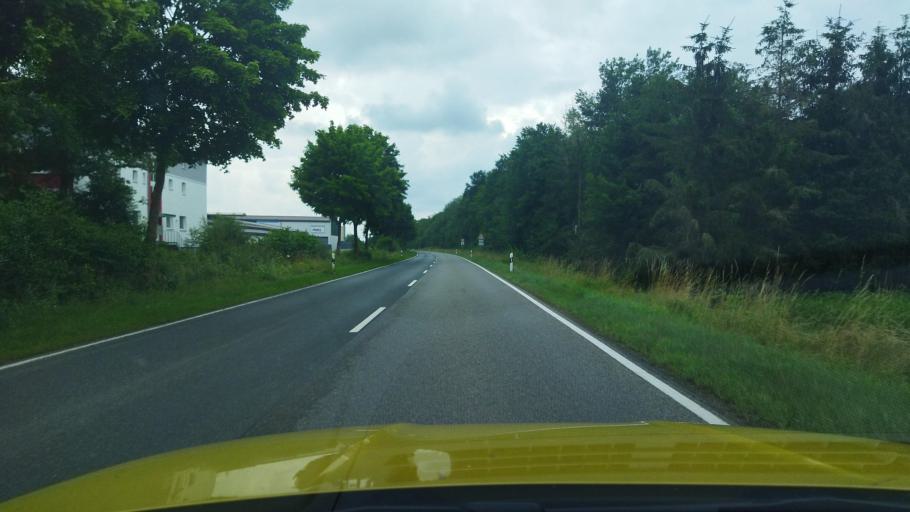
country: DE
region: Bavaria
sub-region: Regierungsbezirk Mittelfranken
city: Gunzenhausen
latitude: 49.1257
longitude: 10.7793
